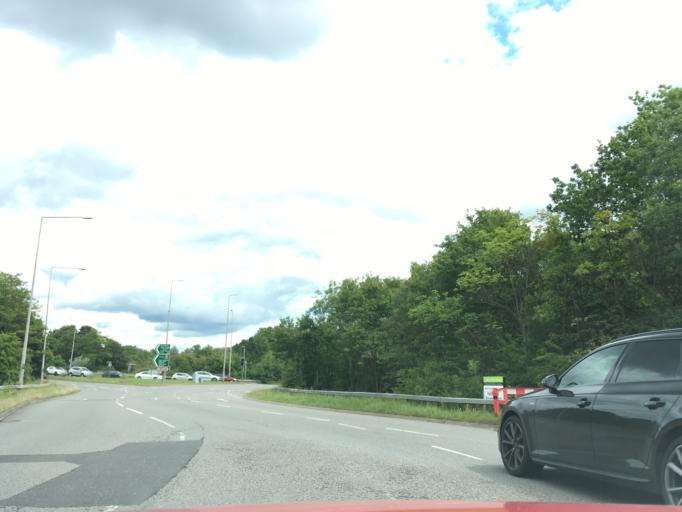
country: GB
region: England
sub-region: Buckinghamshire
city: Bletchley
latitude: 52.0124
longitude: -0.7402
